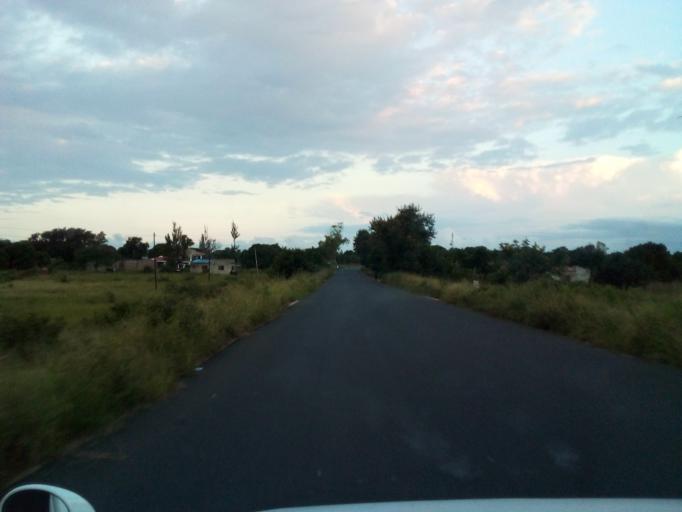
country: MZ
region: Maputo City
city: Maputo
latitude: -26.3389
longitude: 32.6694
